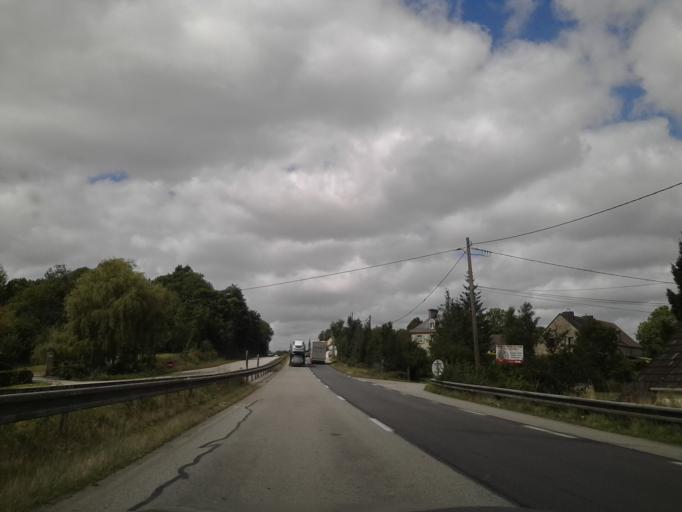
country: FR
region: Lower Normandy
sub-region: Departement de la Manche
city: Valognes
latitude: 49.5248
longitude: -1.5082
